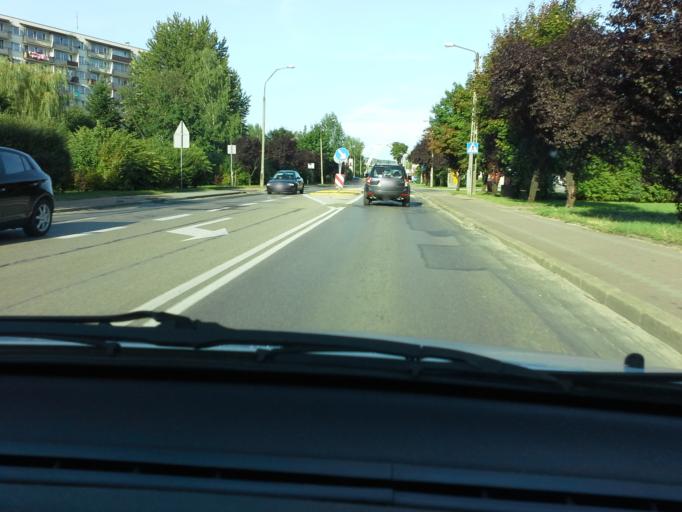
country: PL
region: Lesser Poland Voivodeship
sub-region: Powiat chrzanowski
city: Chrzanow
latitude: 50.1440
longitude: 19.4168
